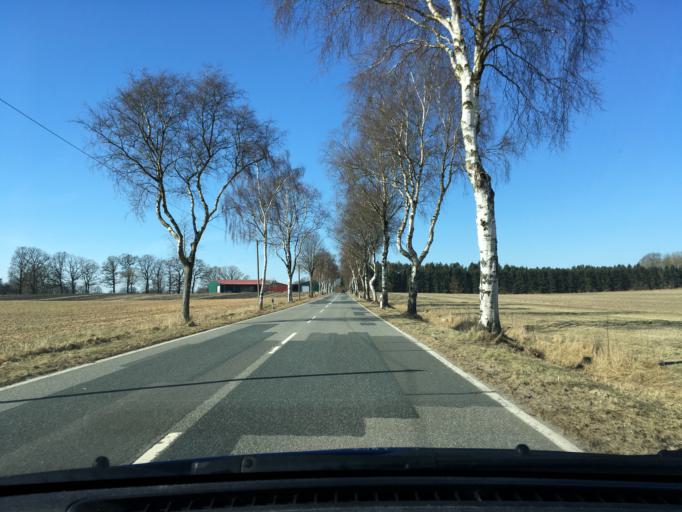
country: DE
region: Lower Saxony
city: Egestorf
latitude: 53.1522
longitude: 10.0792
